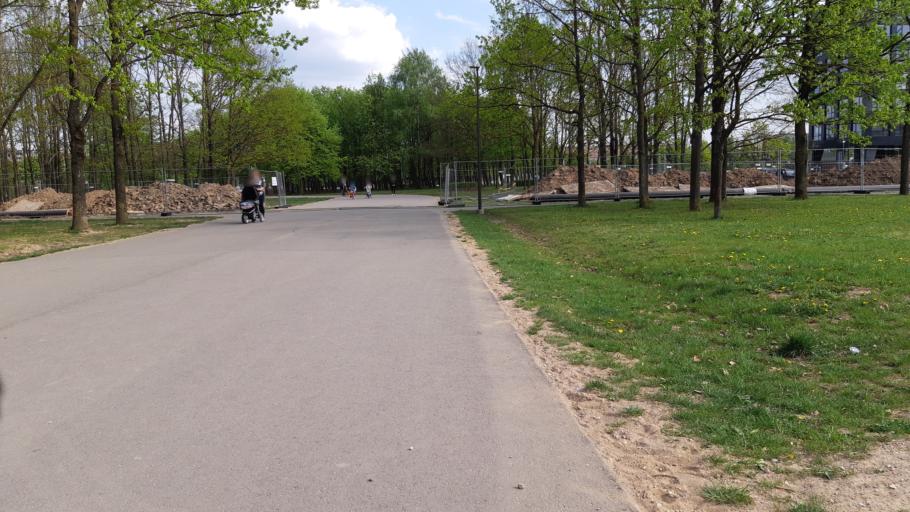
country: LT
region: Kauno apskritis
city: Dainava (Kaunas)
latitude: 54.9220
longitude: 23.9530
